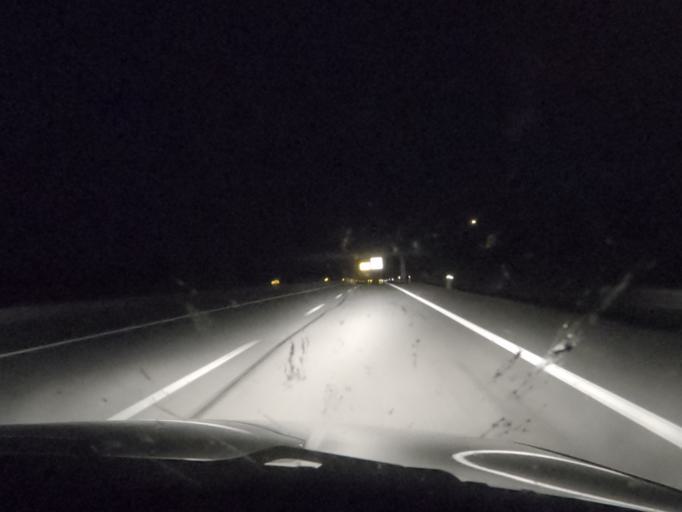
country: PT
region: Evora
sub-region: Estremoz
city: Estremoz
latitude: 38.8297
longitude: -7.6113
